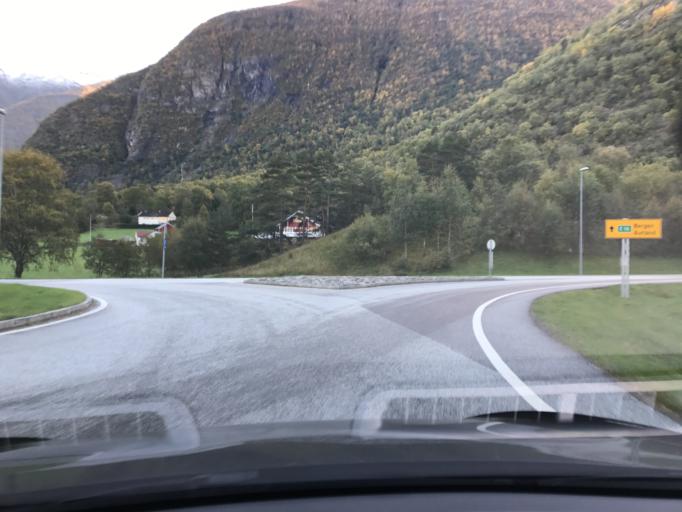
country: NO
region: Sogn og Fjordane
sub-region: Laerdal
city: Laerdalsoyri
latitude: 61.0650
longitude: 7.5057
